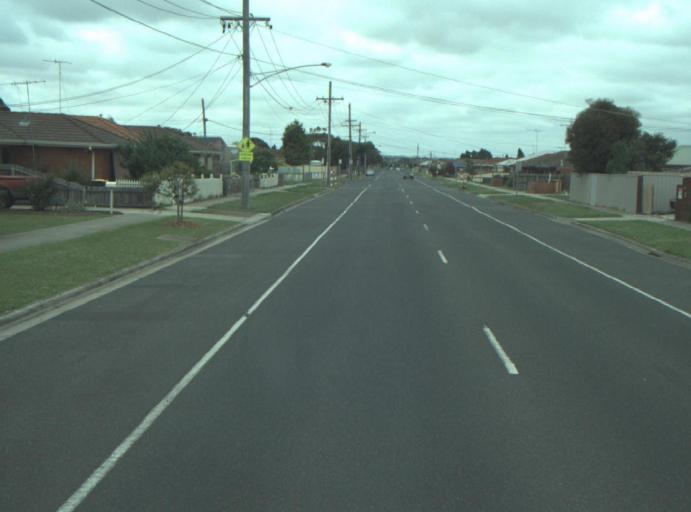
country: AU
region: Victoria
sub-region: Greater Geelong
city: Bell Post Hill
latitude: -38.0684
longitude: 144.3493
